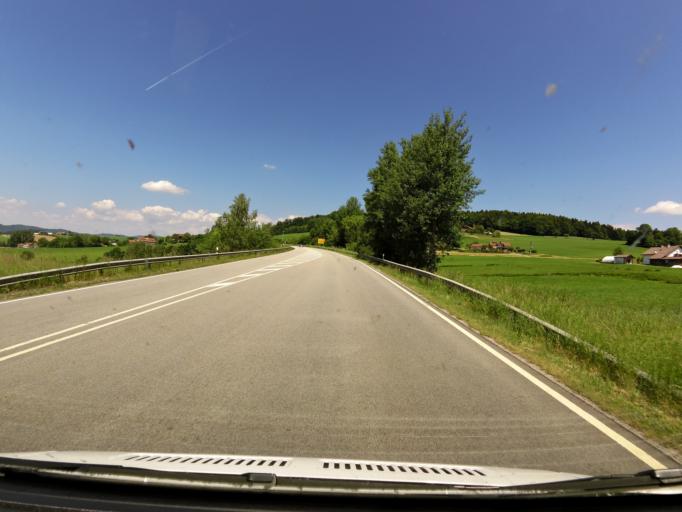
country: DE
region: Bavaria
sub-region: Lower Bavaria
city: Roehrnbach
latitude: 48.7532
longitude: 13.5153
